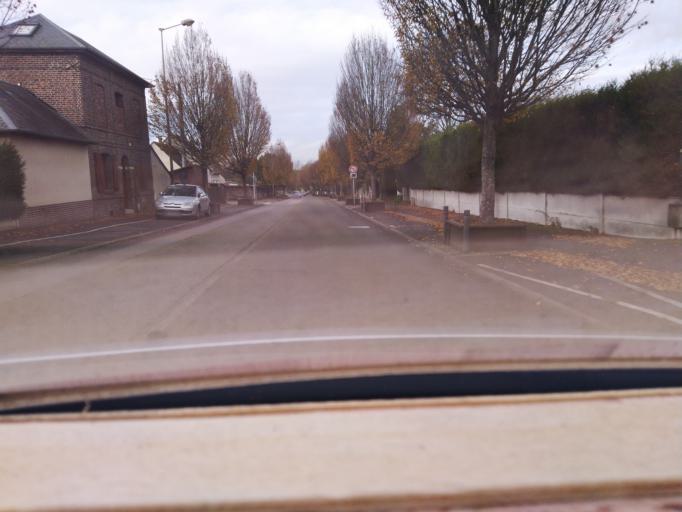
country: FR
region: Haute-Normandie
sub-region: Departement de la Seine-Maritime
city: Canteleu
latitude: 49.4415
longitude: 1.0241
